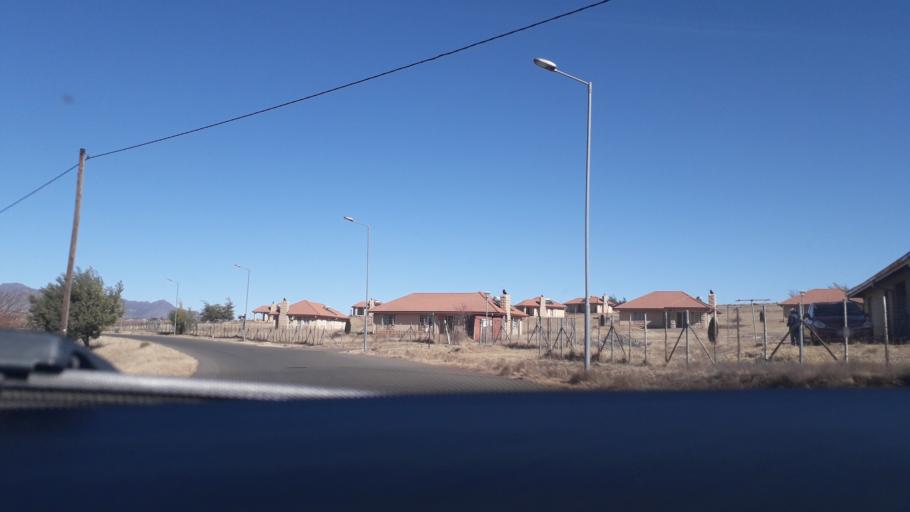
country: LS
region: Berea
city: Teyateyaneng
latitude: -29.3275
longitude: 27.7727
